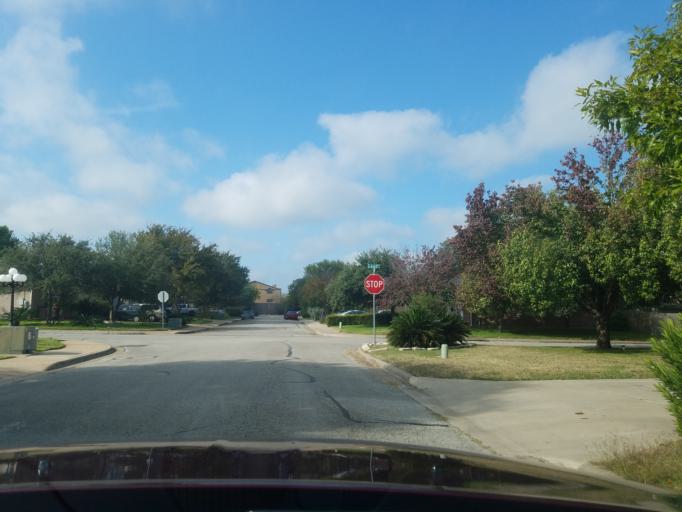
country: US
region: Texas
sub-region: Williamson County
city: Jollyville
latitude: 30.4584
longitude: -97.7848
